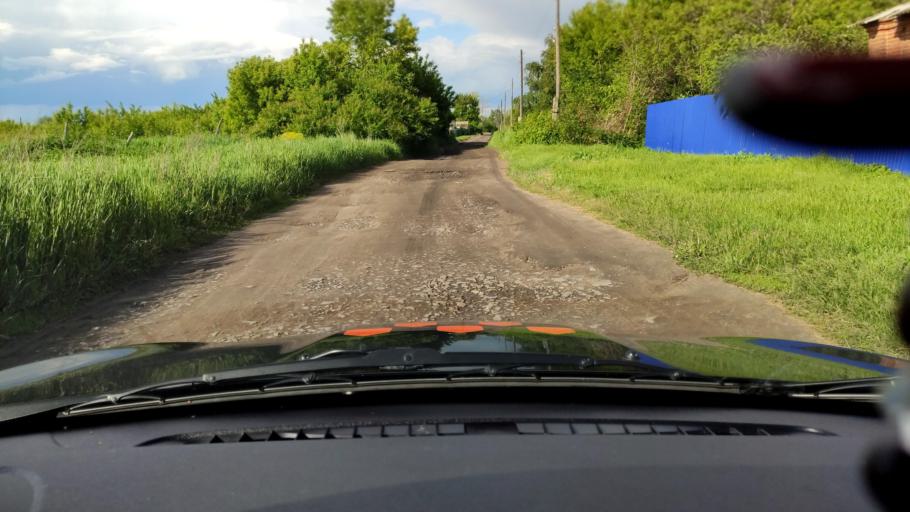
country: RU
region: Voronezj
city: Uryv-Pokrovka
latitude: 51.1126
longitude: 39.1770
